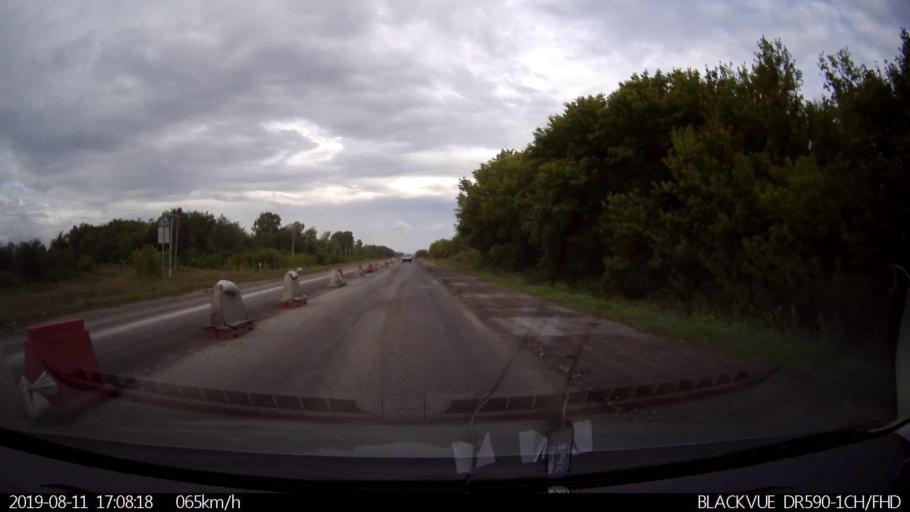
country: RU
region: Ulyanovsk
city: Mayna
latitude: 54.2924
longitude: 47.8376
